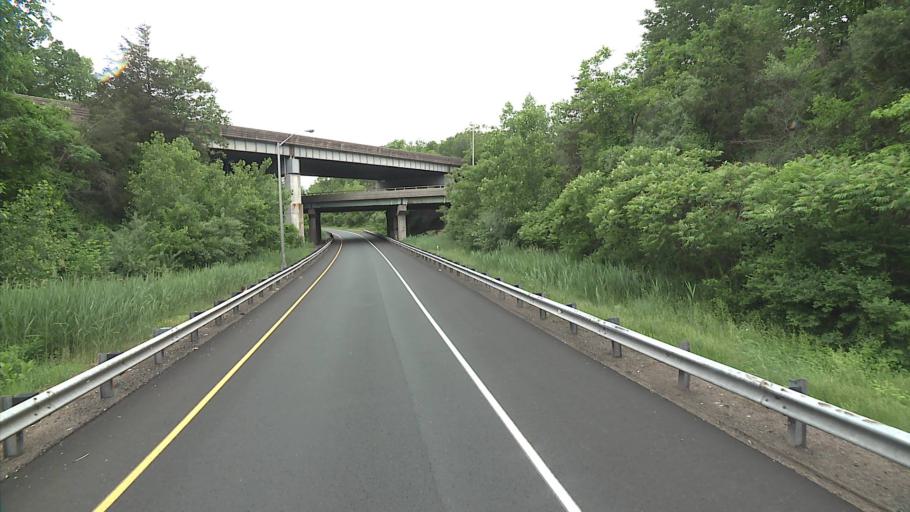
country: US
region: Connecticut
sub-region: Middlesex County
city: Cromwell
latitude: 41.6238
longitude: -72.6934
